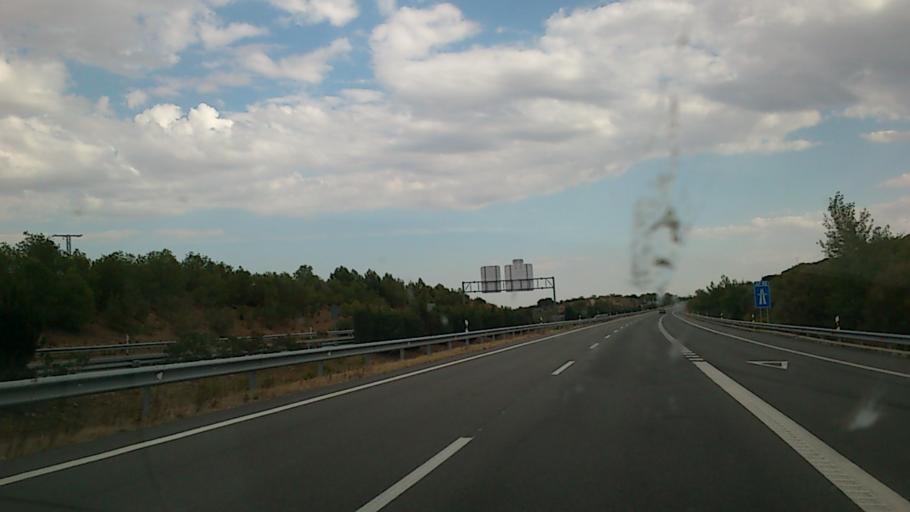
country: ES
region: Navarre
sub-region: Provincia de Navarra
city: Sartaguda
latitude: 42.3683
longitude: -2.0761
